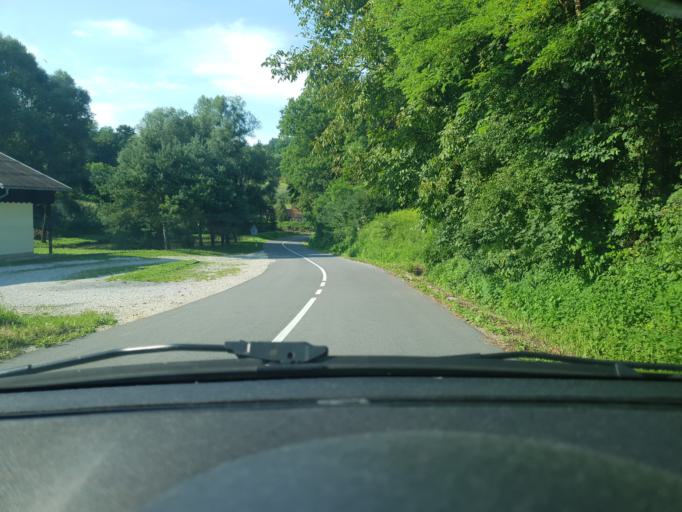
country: HR
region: Krapinsko-Zagorska
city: Pregrada
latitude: 46.0751
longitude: 15.7960
